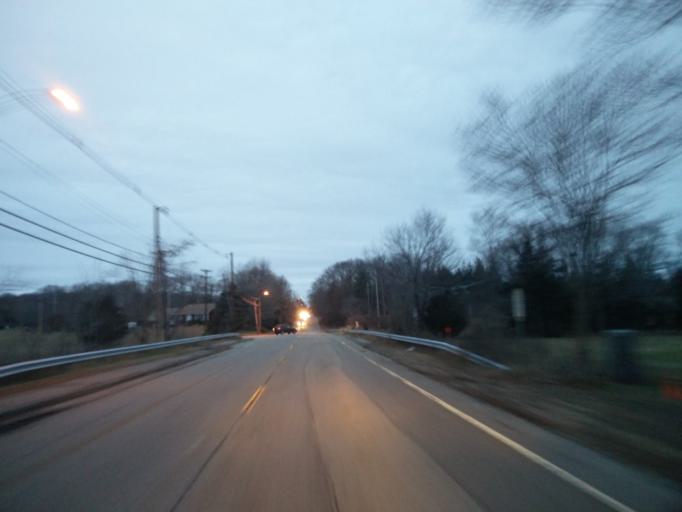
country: US
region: Massachusetts
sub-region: Plymouth County
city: Hingham
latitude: 42.2520
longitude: -70.8599
